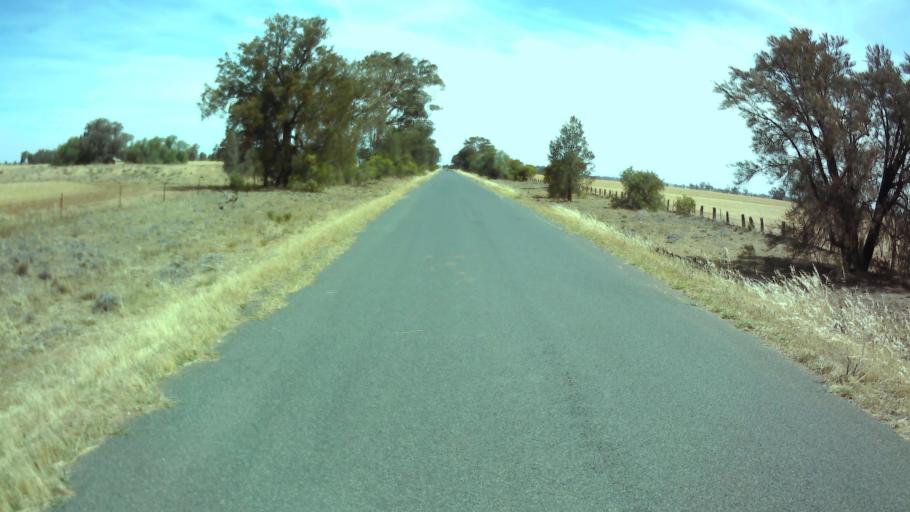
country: AU
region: New South Wales
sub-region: Weddin
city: Grenfell
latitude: -33.9487
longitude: 147.7781
